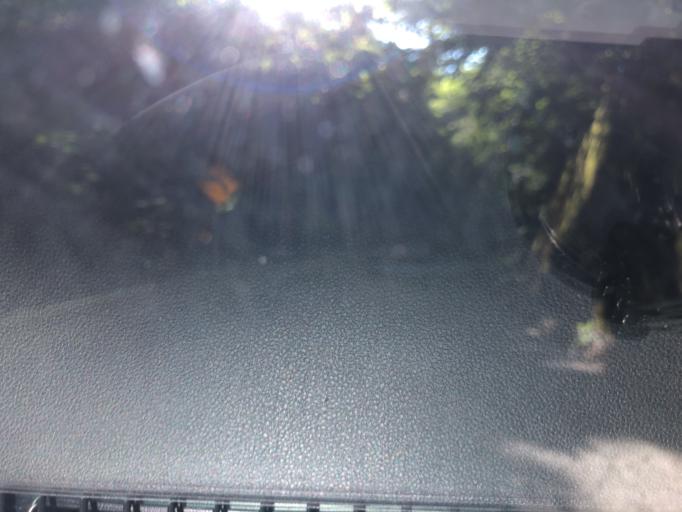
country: JP
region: Ibaraki
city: Kitaibaraki
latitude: 36.8693
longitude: 140.6989
